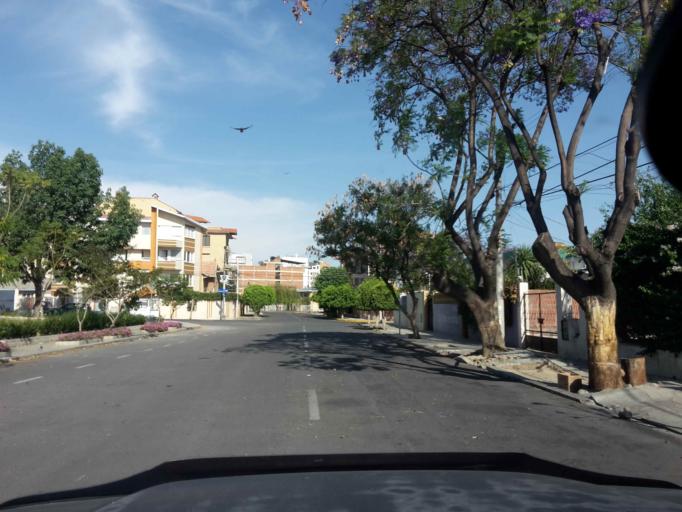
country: BO
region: Cochabamba
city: Cochabamba
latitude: -17.3747
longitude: -66.1700
